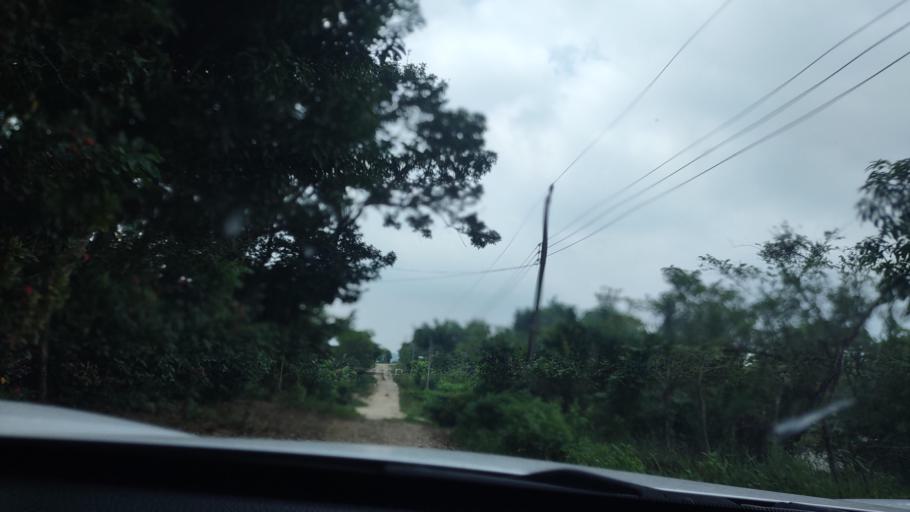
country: MX
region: Veracruz
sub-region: Uxpanapa
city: Poblado 10
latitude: 17.5209
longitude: -94.3028
